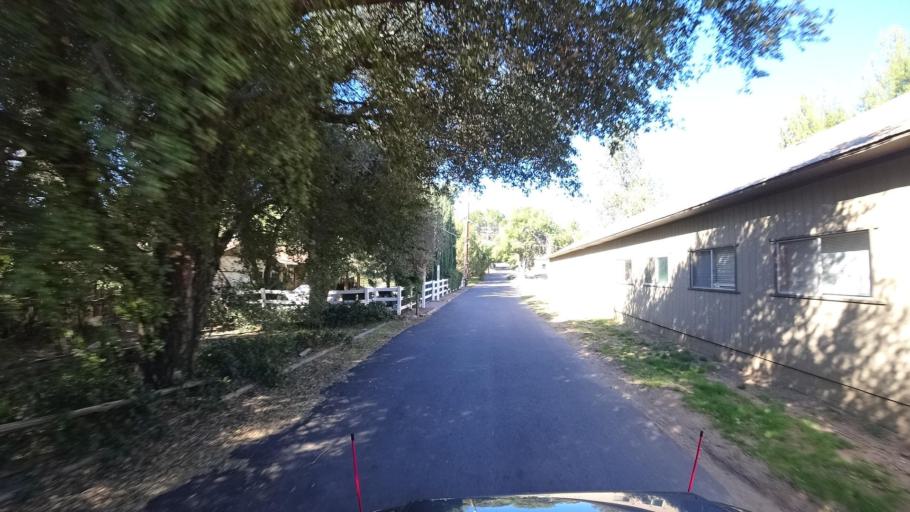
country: US
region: California
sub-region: San Diego County
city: Descanso
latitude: 32.8554
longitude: -116.6234
